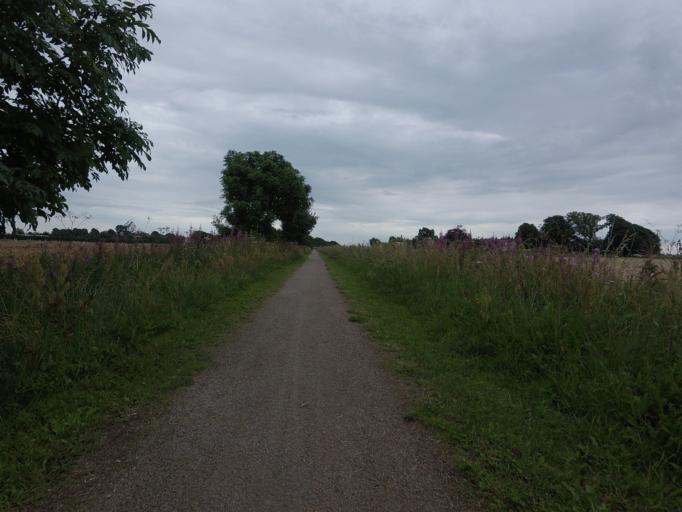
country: DK
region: North Denmark
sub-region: Alborg Kommune
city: Vadum
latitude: 57.1141
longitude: 9.8784
